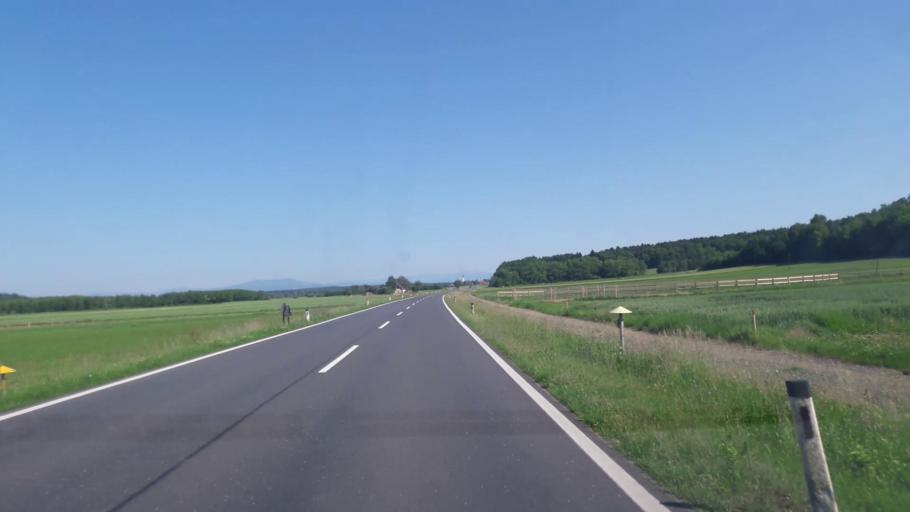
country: AT
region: Burgenland
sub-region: Politischer Bezirk Jennersdorf
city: Rudersdorf
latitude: 47.0627
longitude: 16.1156
